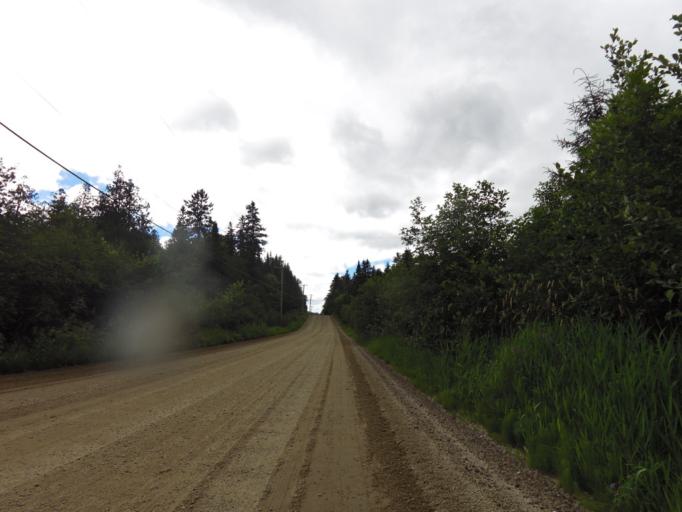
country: CA
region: Quebec
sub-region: Laurentides
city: Mont-Tremblant
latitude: 45.9500
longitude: -74.5941
